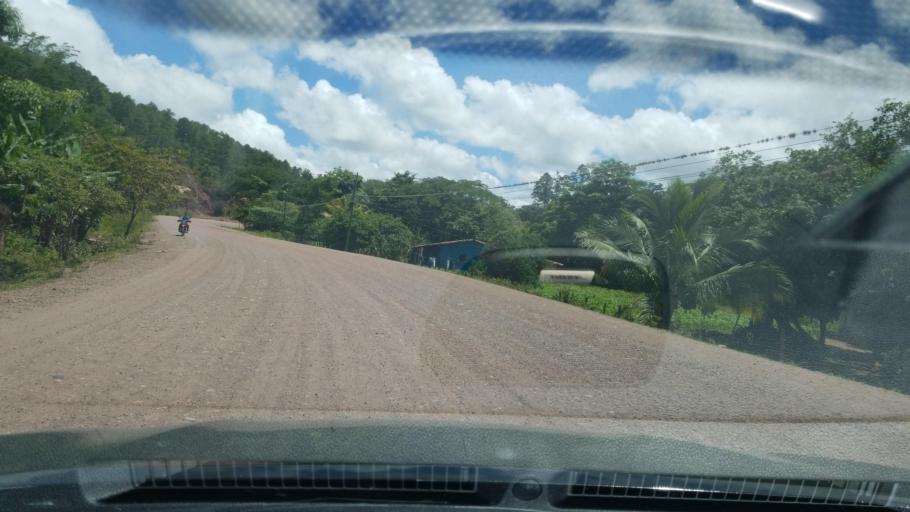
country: HN
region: Francisco Morazan
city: San Juan de Flores
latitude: 14.3388
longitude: -87.0429
